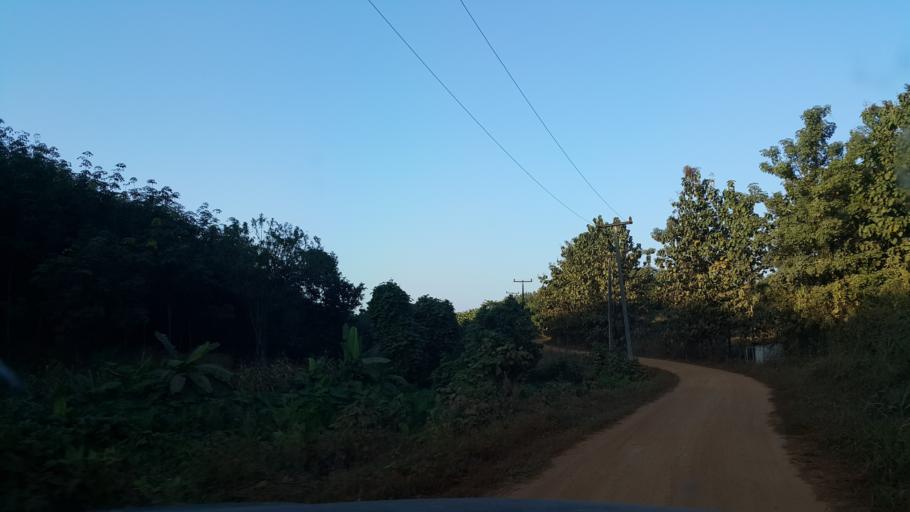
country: TH
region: Sukhothai
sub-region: Amphoe Si Satchanalai
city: Si Satchanalai
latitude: 17.6090
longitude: 99.6194
